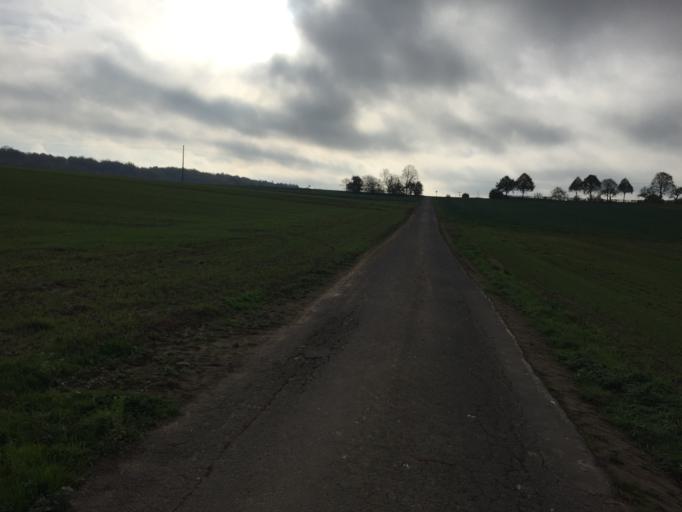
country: DE
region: Hesse
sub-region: Regierungsbezirk Giessen
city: Grunberg
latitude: 50.5967
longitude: 8.9780
